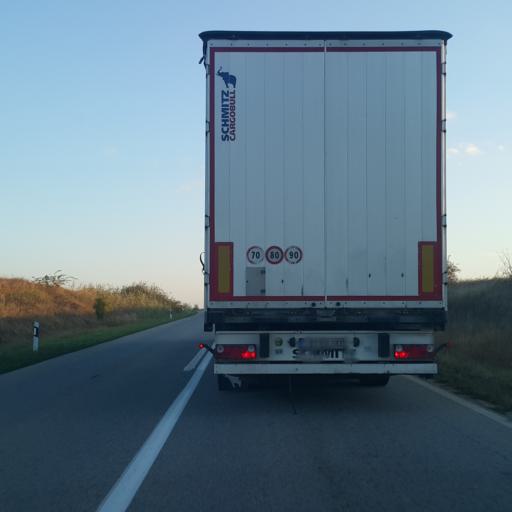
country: RS
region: Central Serbia
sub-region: Zajecarski Okrug
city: Zajecar
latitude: 44.0639
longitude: 22.3341
